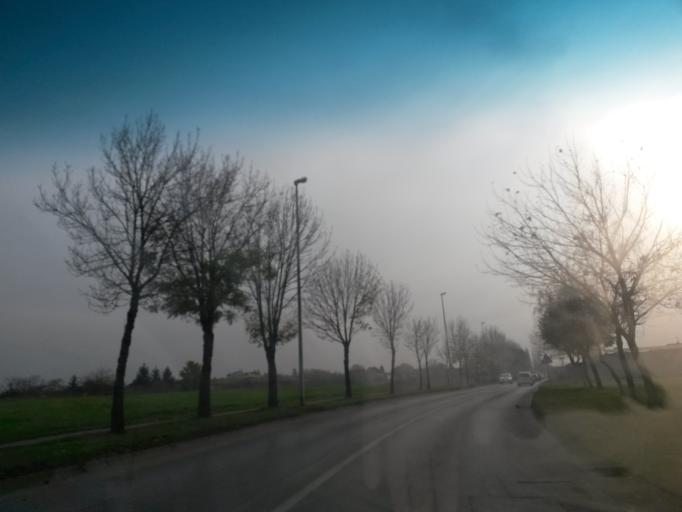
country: HR
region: Vukovarsko-Srijemska
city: Vinkovci
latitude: 45.2895
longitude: 18.8195
